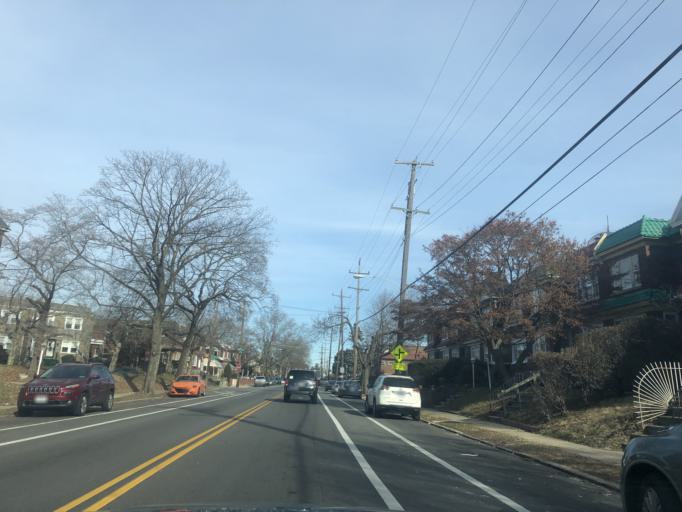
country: US
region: Pennsylvania
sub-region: Montgomery County
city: Wyncote
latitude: 40.0696
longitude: -75.1560
